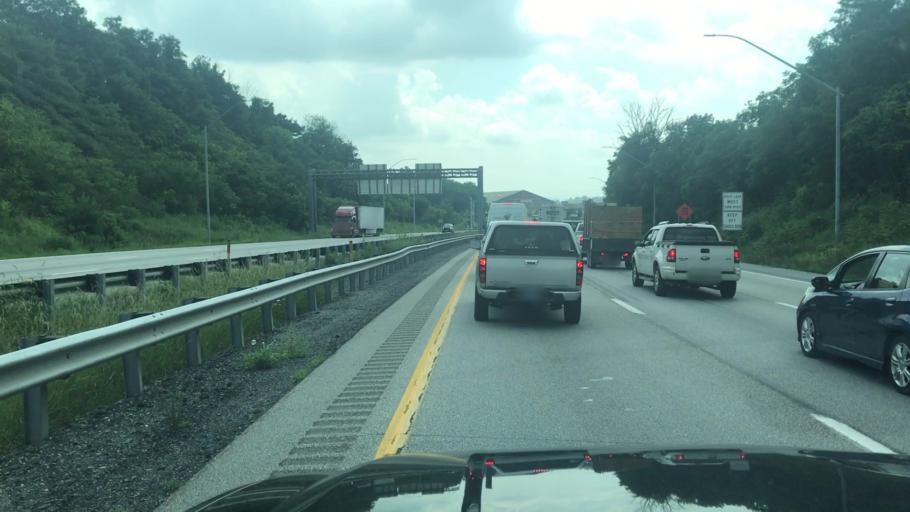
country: US
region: Pennsylvania
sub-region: Dauphin County
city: Harrisburg
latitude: 40.2937
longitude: -76.8813
